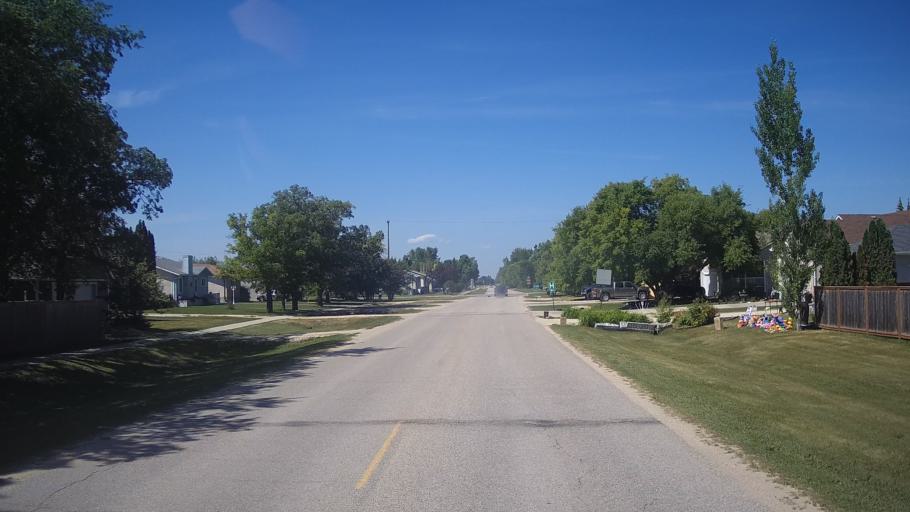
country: CA
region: Manitoba
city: Stonewall
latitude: 50.1289
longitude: -97.3333
